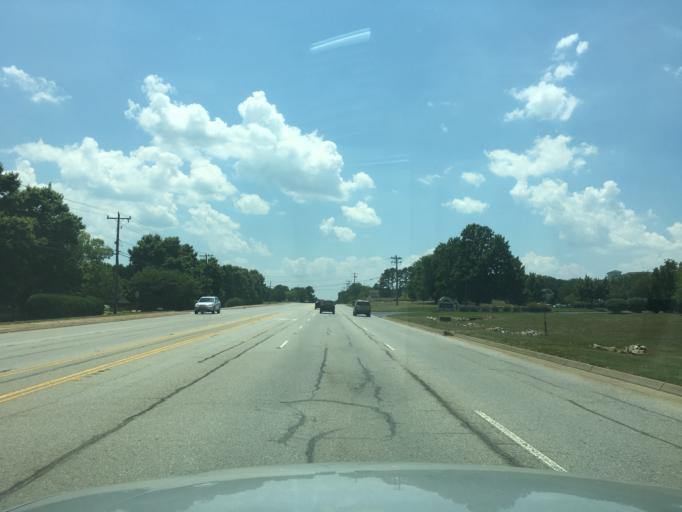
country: US
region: South Carolina
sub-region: Anderson County
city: Northlake
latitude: 34.5911
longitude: -82.6190
